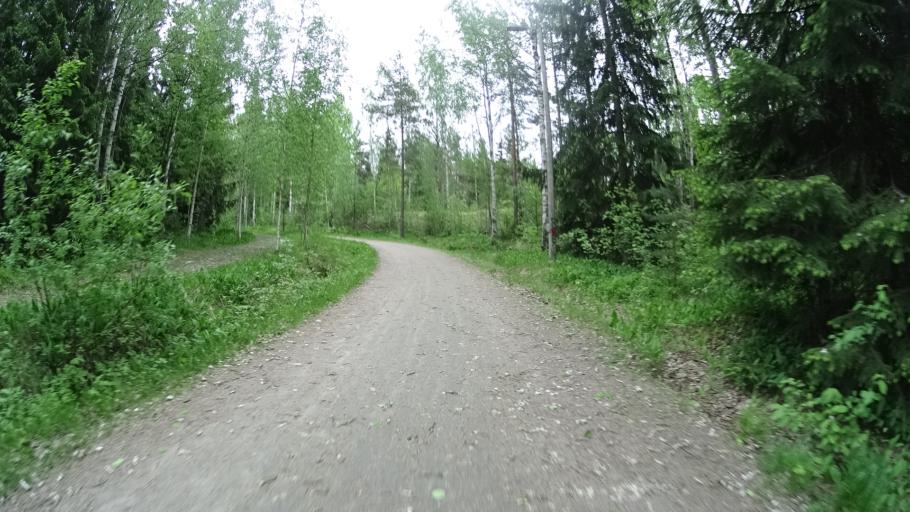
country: FI
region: Uusimaa
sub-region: Helsinki
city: Vantaa
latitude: 60.2496
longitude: 25.0726
